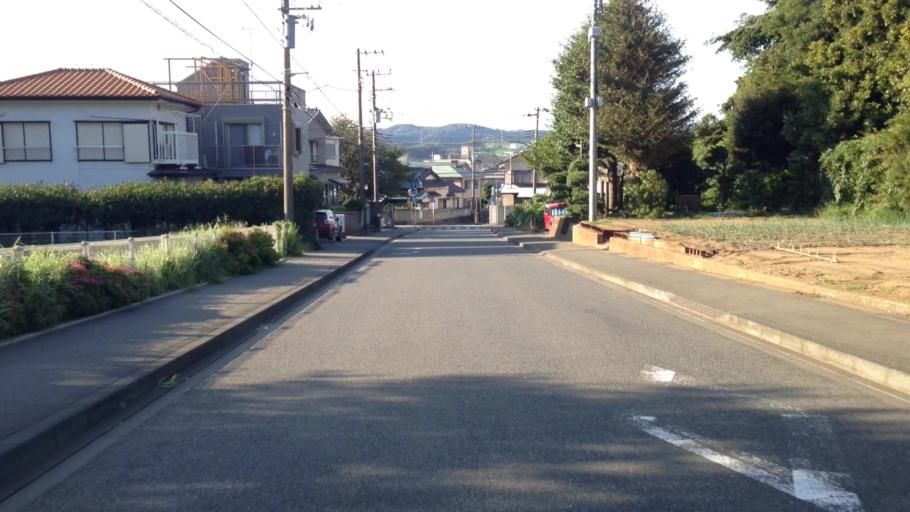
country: JP
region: Kanagawa
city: Miura
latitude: 35.2060
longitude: 139.6156
